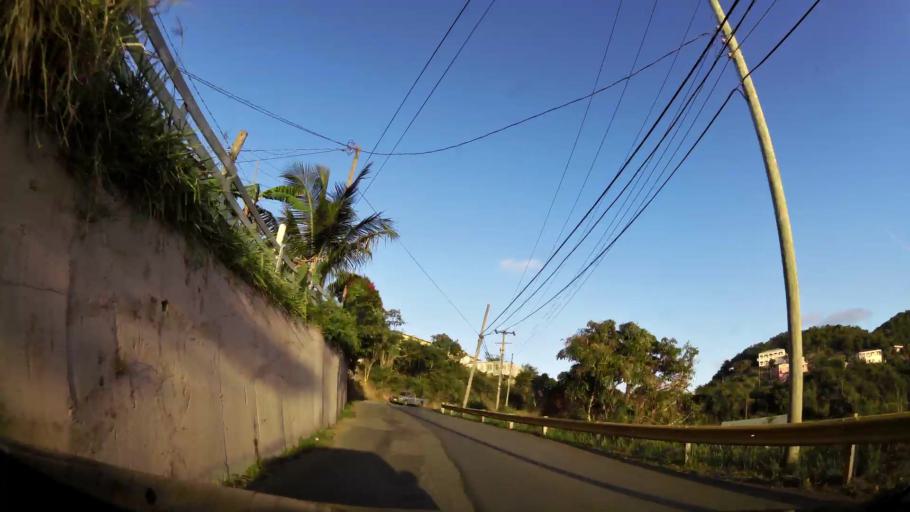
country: VG
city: Tortola
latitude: 18.4427
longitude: -64.6056
